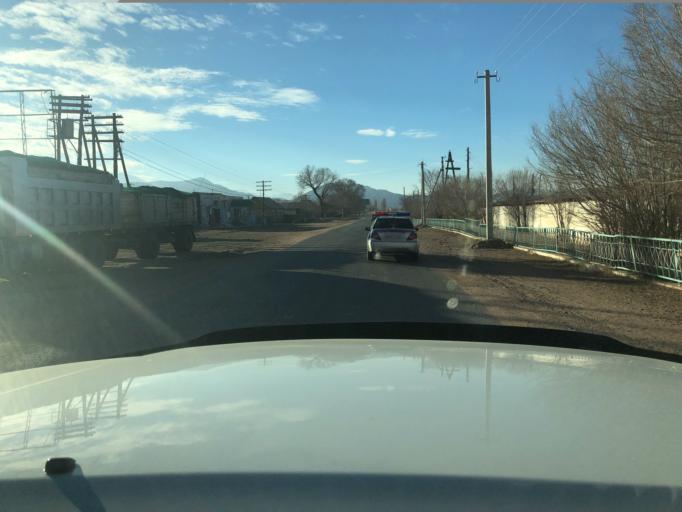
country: KG
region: Ysyk-Koel
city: Bokombayevskoye
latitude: 42.1155
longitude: 76.9838
